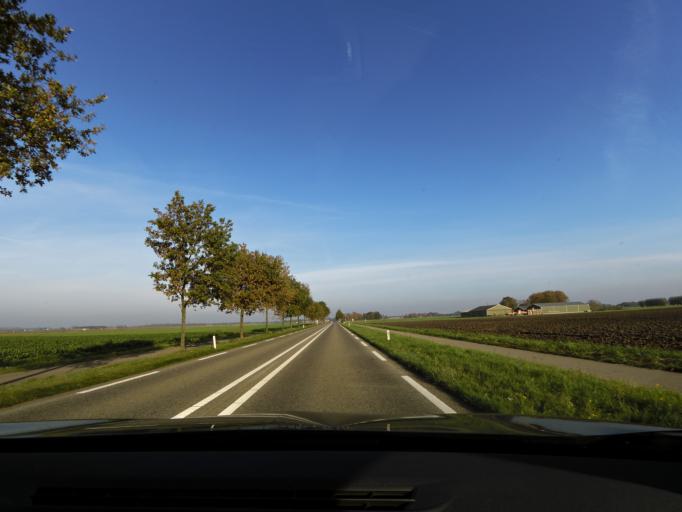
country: NL
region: North Brabant
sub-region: Gemeente Made en Drimmelen
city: Made
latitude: 51.6651
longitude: 4.7217
